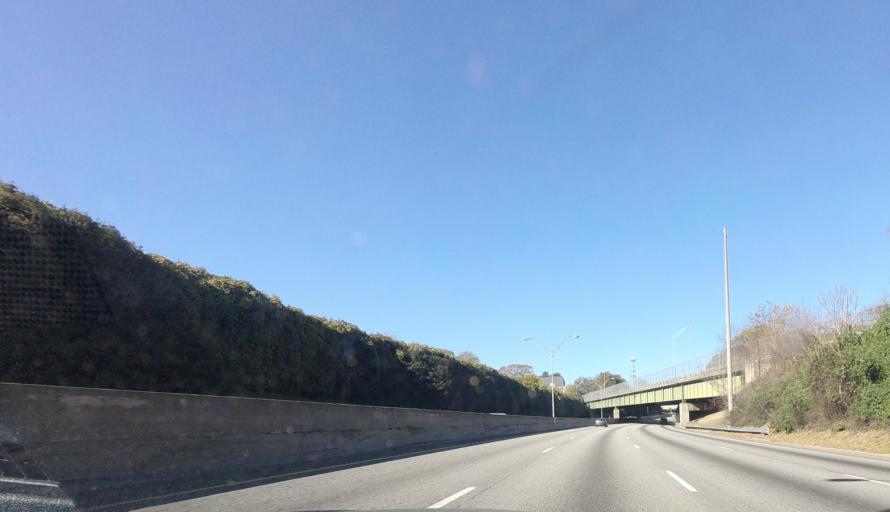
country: US
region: Georgia
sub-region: Fulton County
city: Atlanta
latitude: 33.7472
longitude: -84.4373
